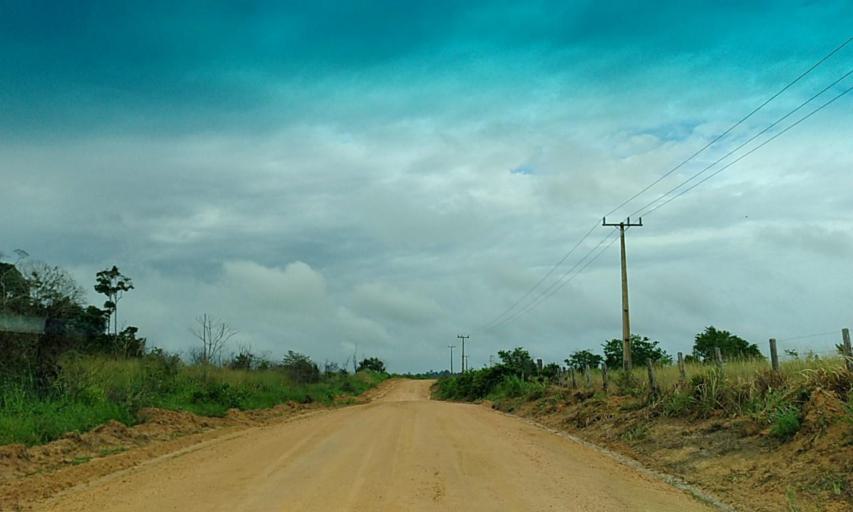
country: BR
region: Para
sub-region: Senador Jose Porfirio
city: Senador Jose Porfirio
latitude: -3.0398
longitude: -51.6787
